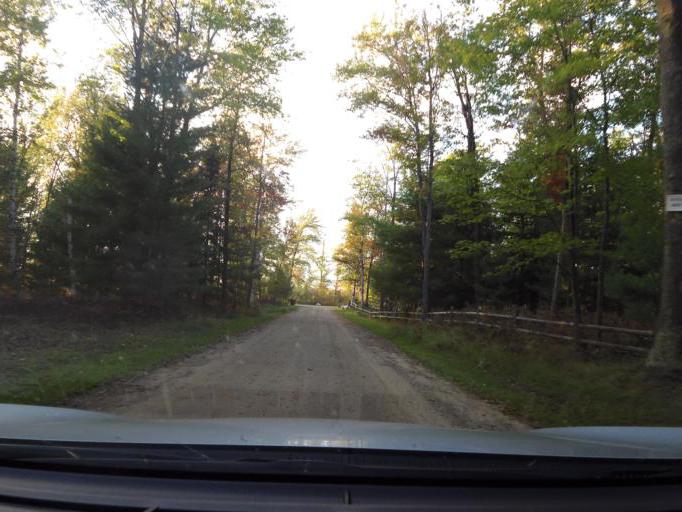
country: US
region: Michigan
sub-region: Roscommon County
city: Saint Helen
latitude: 44.3588
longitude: -84.4706
